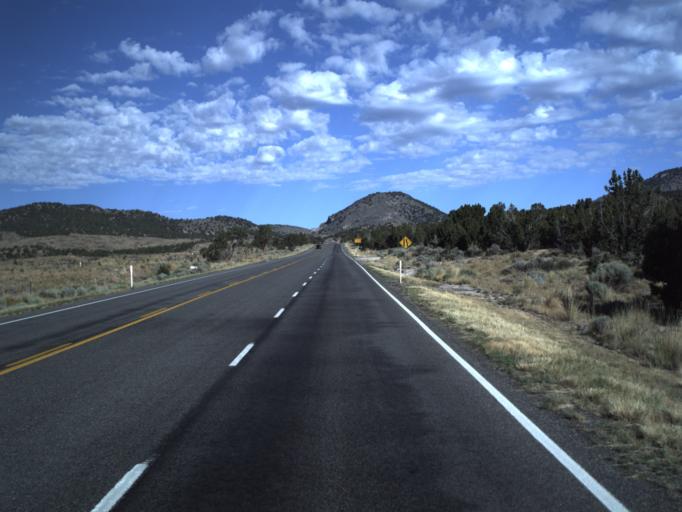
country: US
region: Utah
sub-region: Utah County
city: Genola
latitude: 39.9631
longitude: -112.0430
